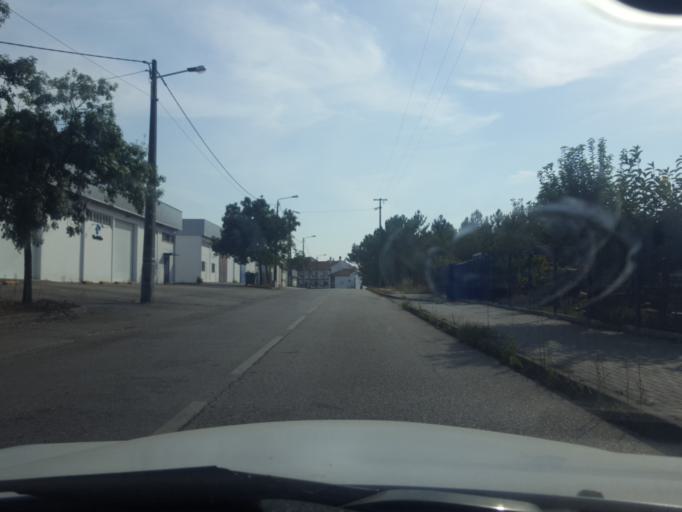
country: PT
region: Leiria
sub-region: Leiria
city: Leiria
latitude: 39.7324
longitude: -8.7617
